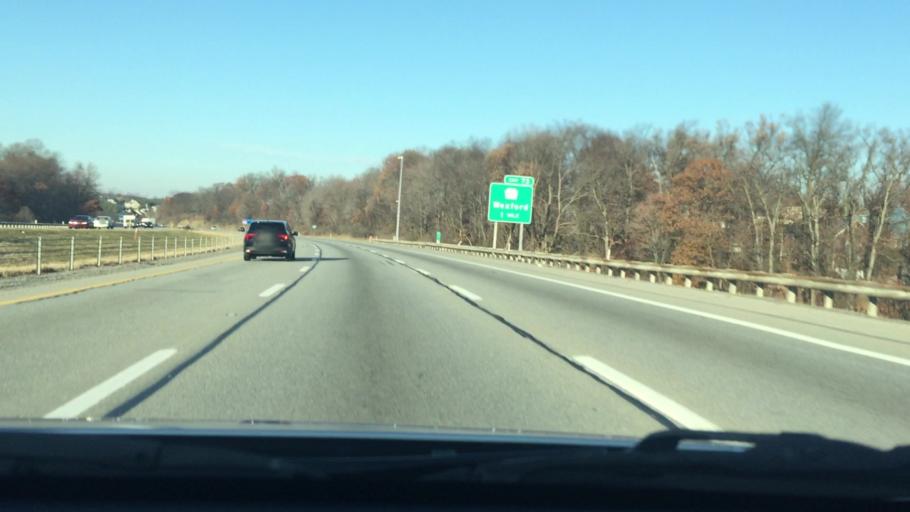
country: US
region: Pennsylvania
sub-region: Allegheny County
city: Franklin Park
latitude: 40.5959
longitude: -80.0940
